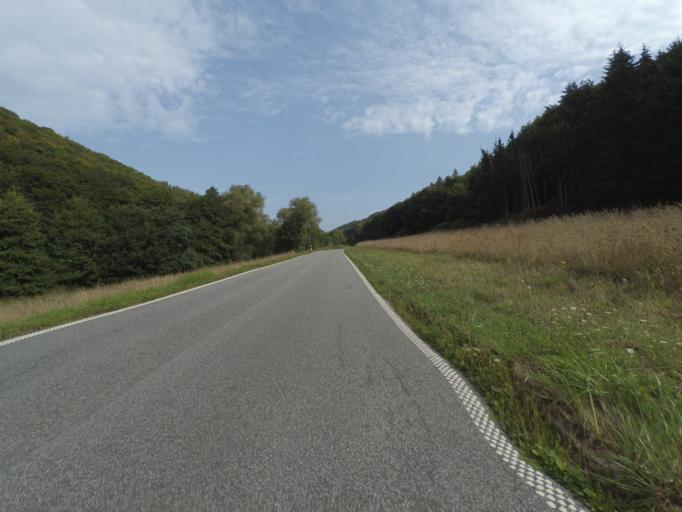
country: DE
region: Rheinland-Pfalz
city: Tawern
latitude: 49.6609
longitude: 6.5122
